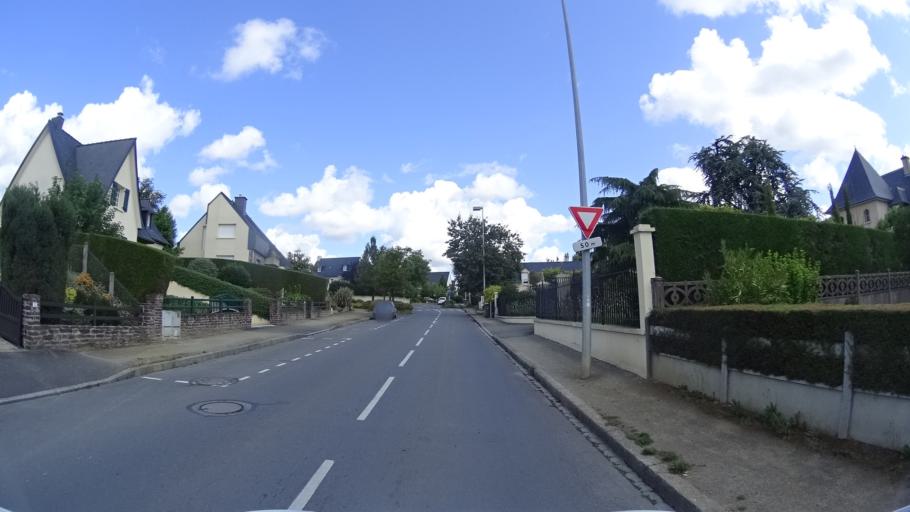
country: FR
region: Brittany
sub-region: Departement d'Ille-et-Vilaine
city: Chartres-de-Bretagne
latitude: 48.0383
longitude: -1.6972
